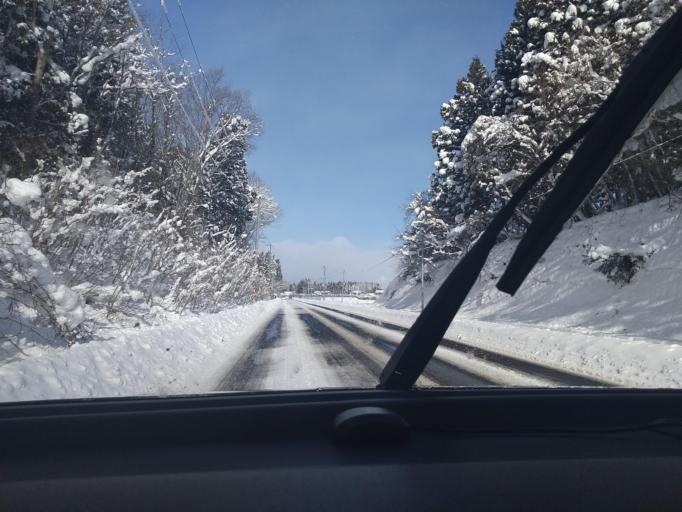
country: JP
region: Iwate
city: Kitakami
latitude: 39.3300
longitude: 141.0392
